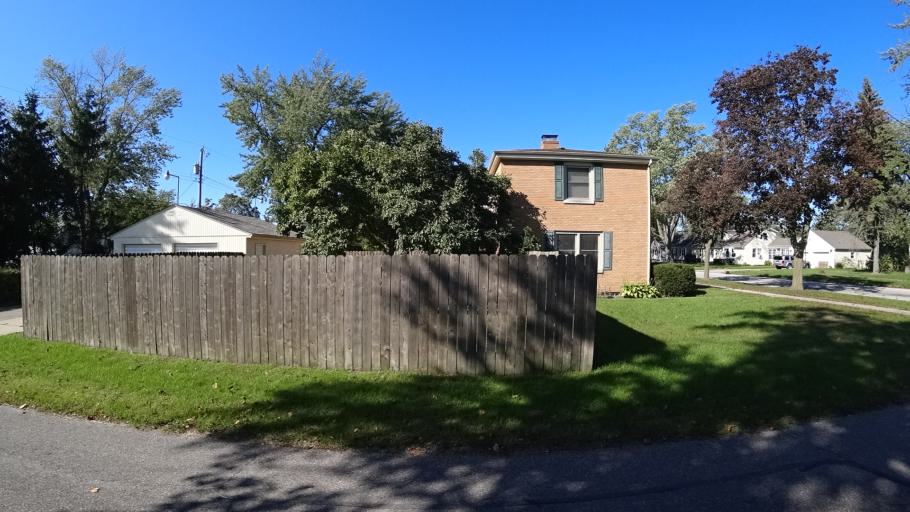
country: US
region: Indiana
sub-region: LaPorte County
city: Michigan City
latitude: 41.7089
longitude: -86.8879
